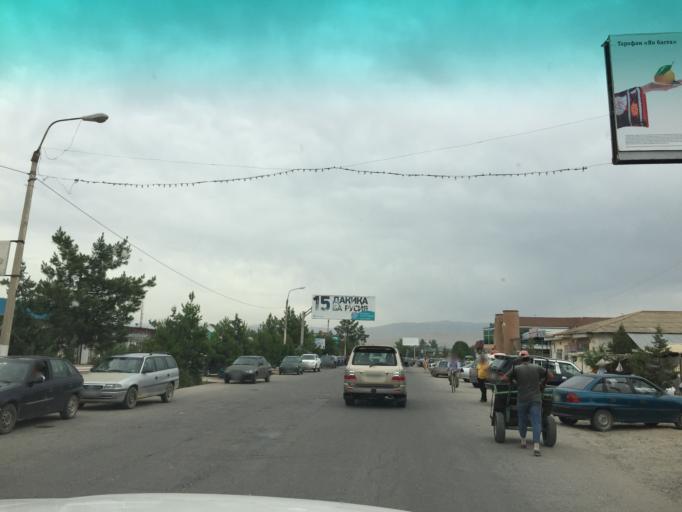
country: TJ
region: Khatlon
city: Vose'
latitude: 37.8054
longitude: 69.6392
